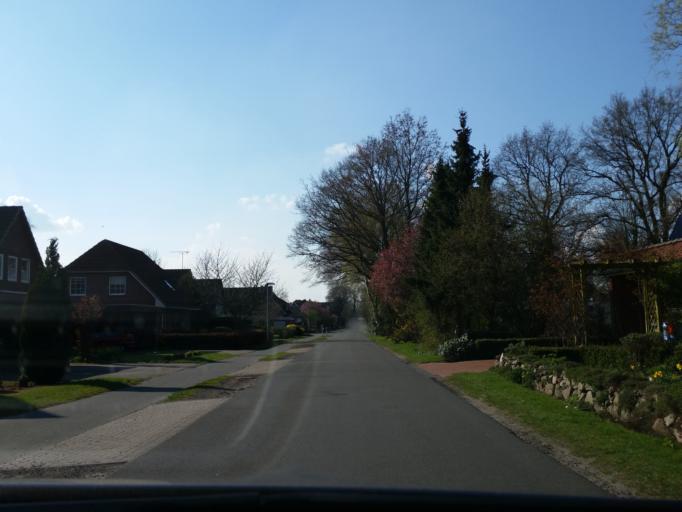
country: DE
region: Lower Saxony
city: Selsingen
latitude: 53.3755
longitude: 9.2239
